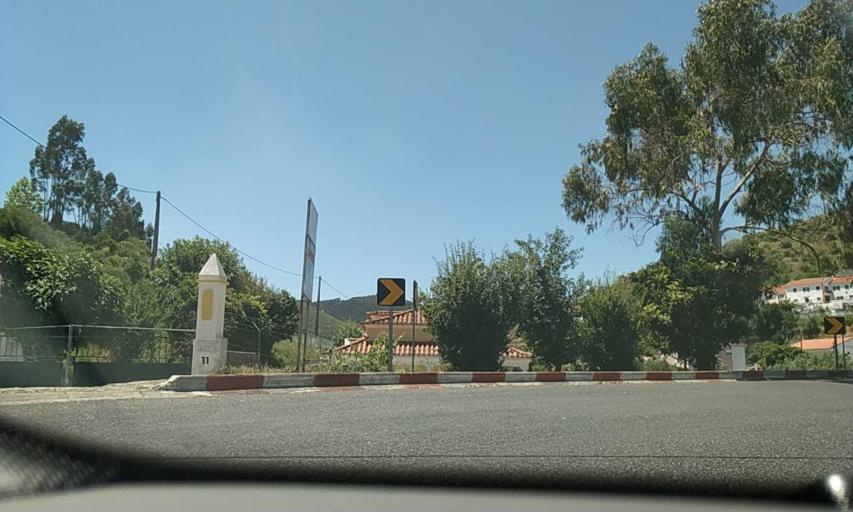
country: PT
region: Lisbon
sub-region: Odivelas
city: Canecas
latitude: 38.8658
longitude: -9.2131
